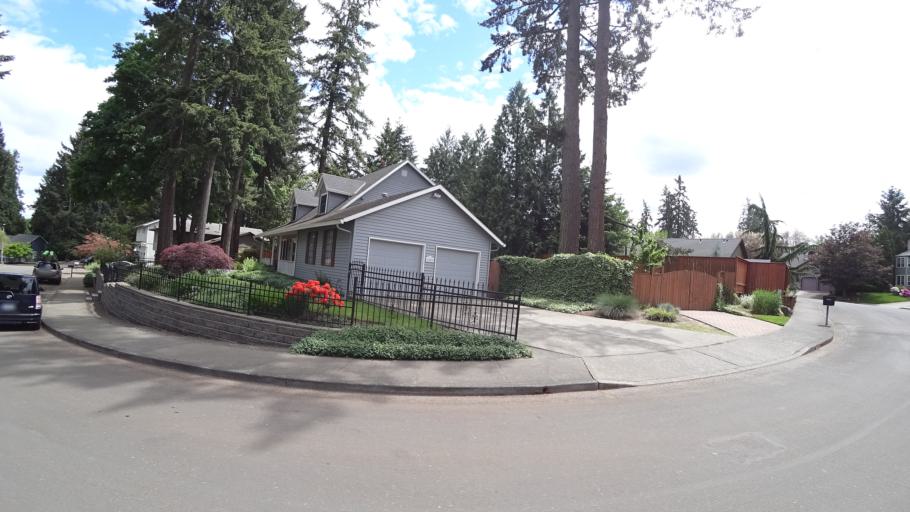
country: US
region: Oregon
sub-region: Washington County
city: Aloha
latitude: 45.4719
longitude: -122.8580
